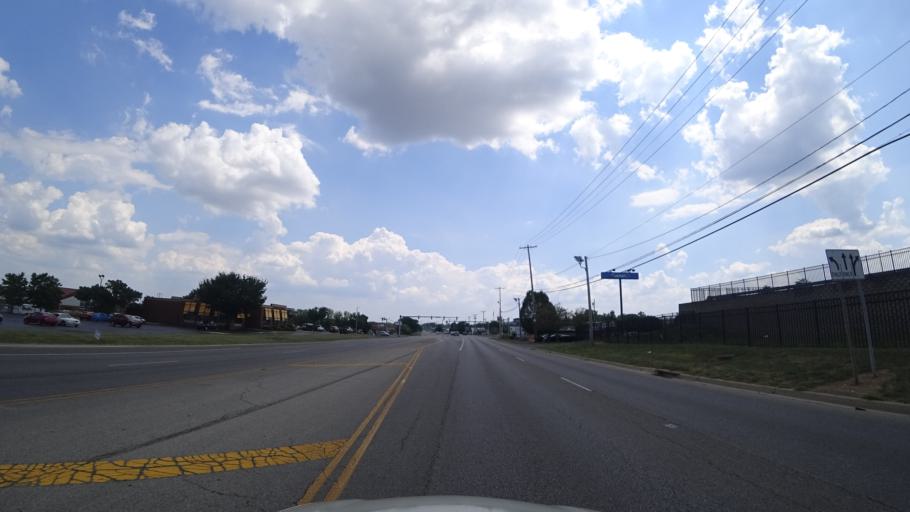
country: US
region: Ohio
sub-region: Butler County
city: Hamilton
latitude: 39.4269
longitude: -84.5974
